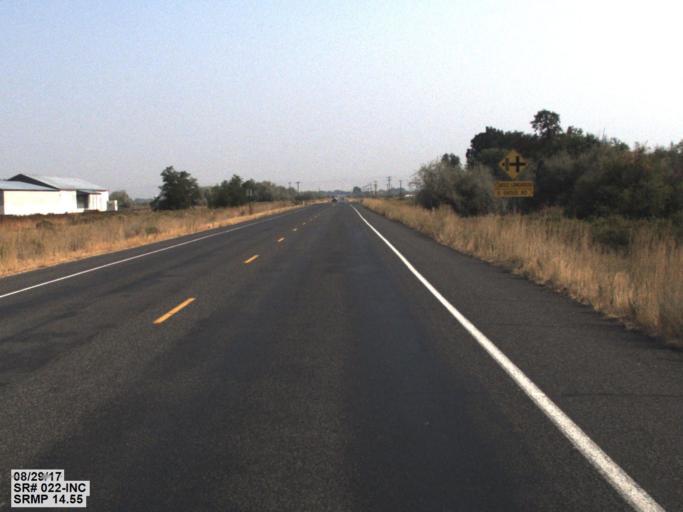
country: US
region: Washington
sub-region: Yakima County
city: Granger
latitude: 46.2722
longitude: -120.1528
